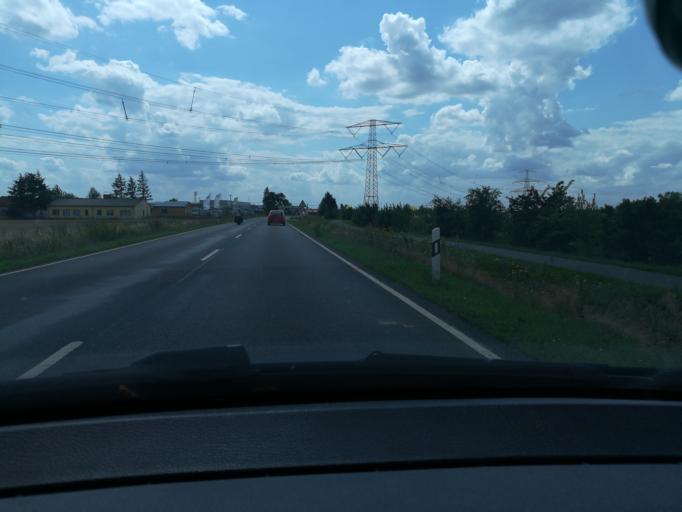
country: DE
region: Saxony-Anhalt
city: Wolmirstedt
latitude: 52.2668
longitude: 11.6434
